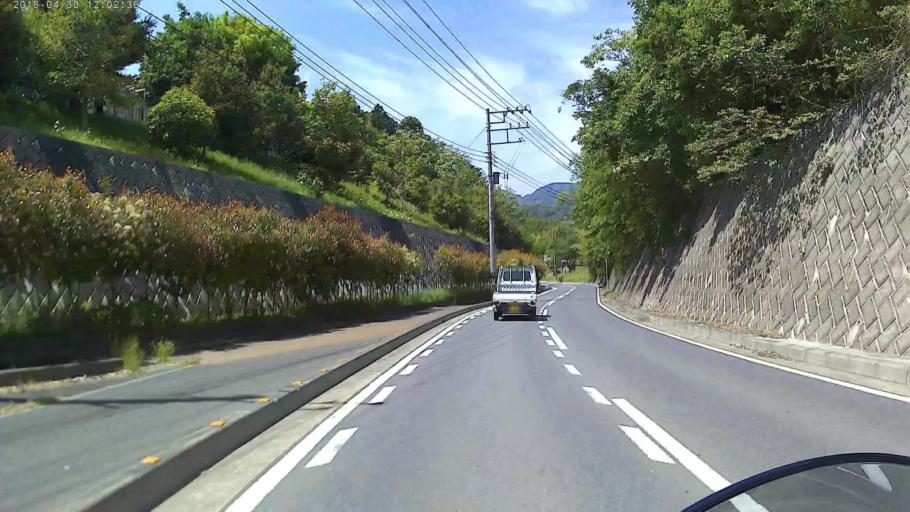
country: JP
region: Kanagawa
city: Zama
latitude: 35.5221
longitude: 139.3164
